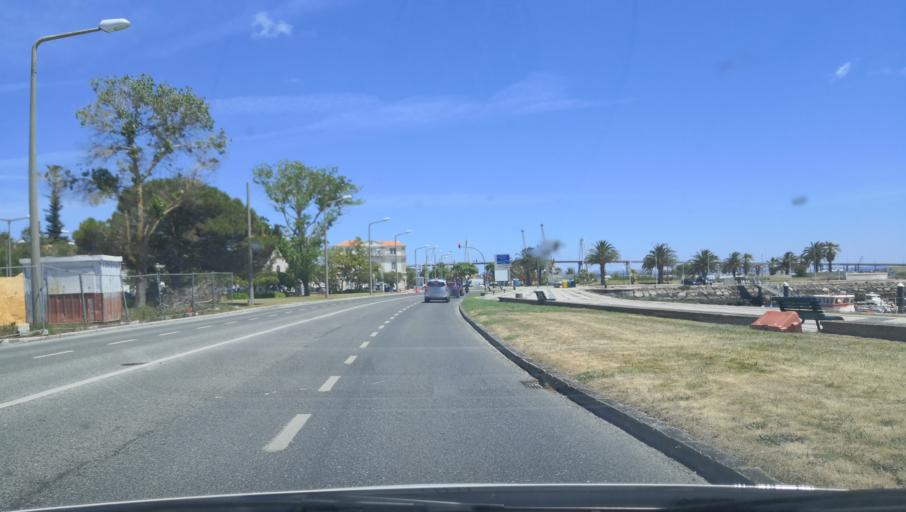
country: PT
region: Coimbra
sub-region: Figueira da Foz
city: Figueira da Foz
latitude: 40.1484
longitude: -8.8580
